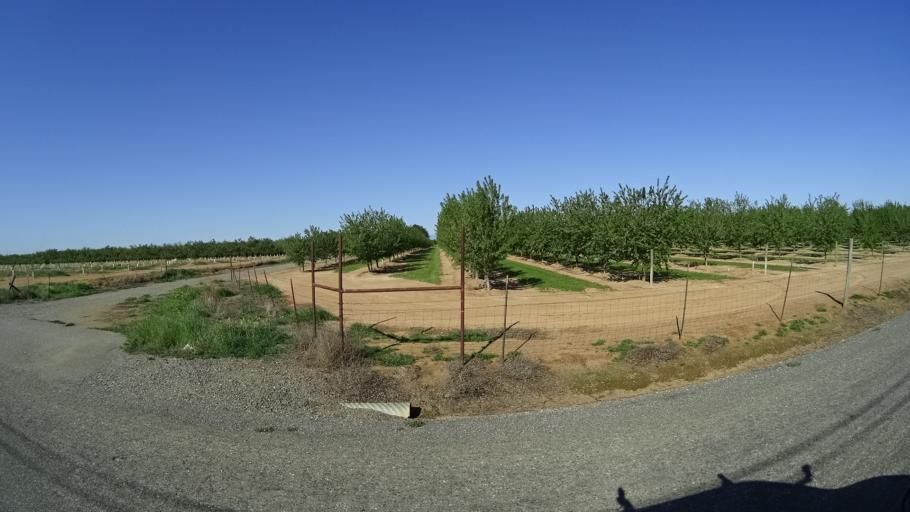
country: US
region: California
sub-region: Glenn County
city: Hamilton City
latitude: 39.7794
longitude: -122.0666
